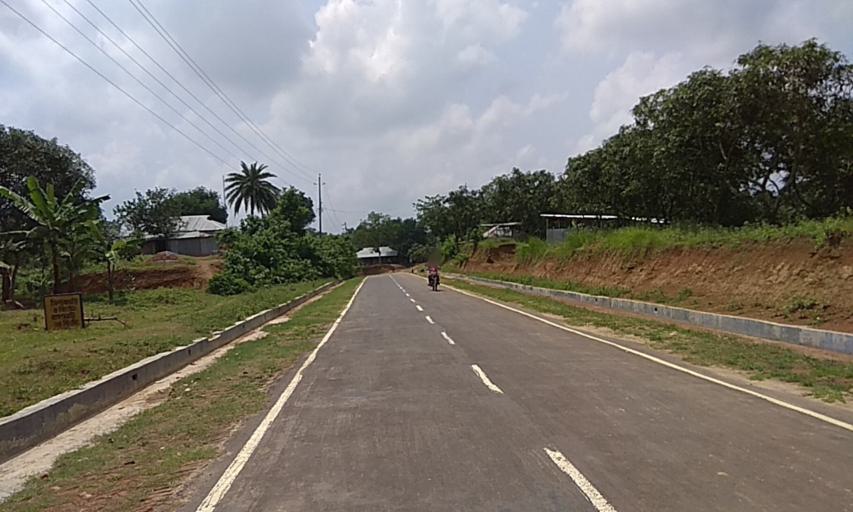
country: BD
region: Chittagong
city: Manikchari
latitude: 22.9361
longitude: 91.8945
